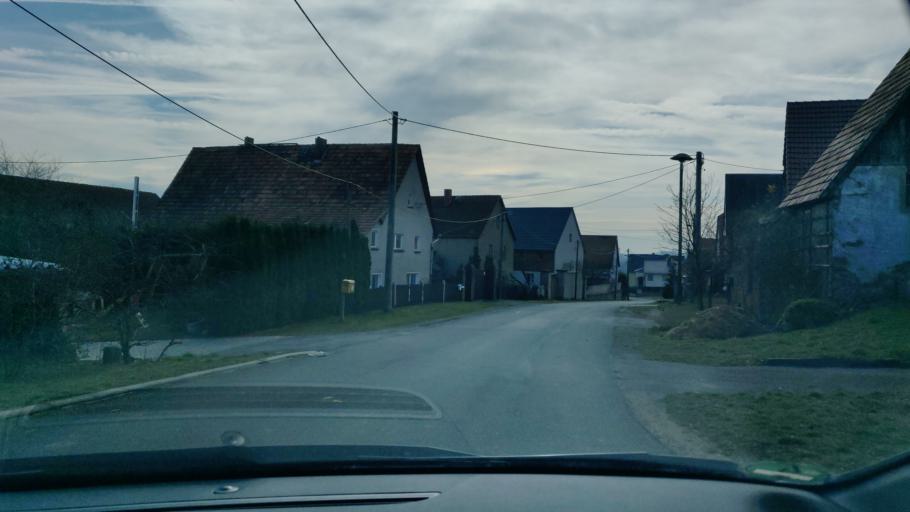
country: DE
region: Saxony
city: Colditz
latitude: 51.0904
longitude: 12.8031
